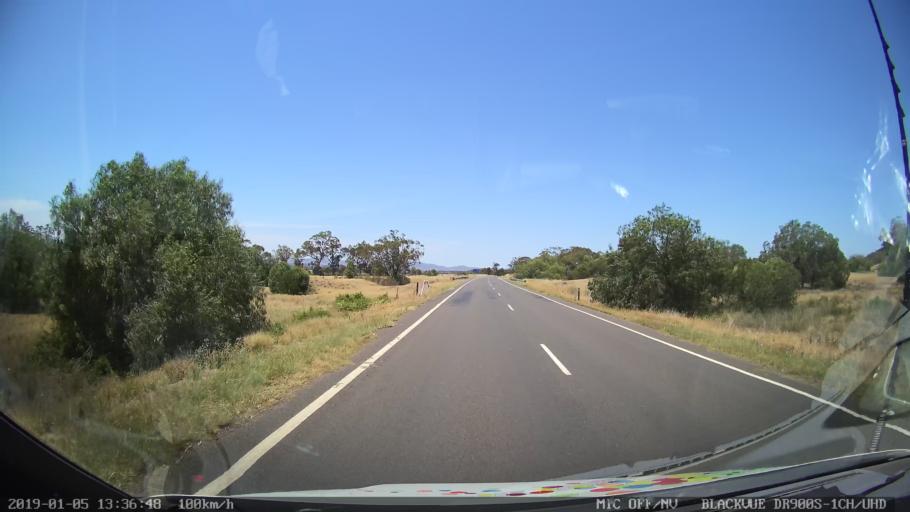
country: AU
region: New South Wales
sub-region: Gunnedah
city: Gunnedah
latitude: -30.9830
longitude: 150.1705
